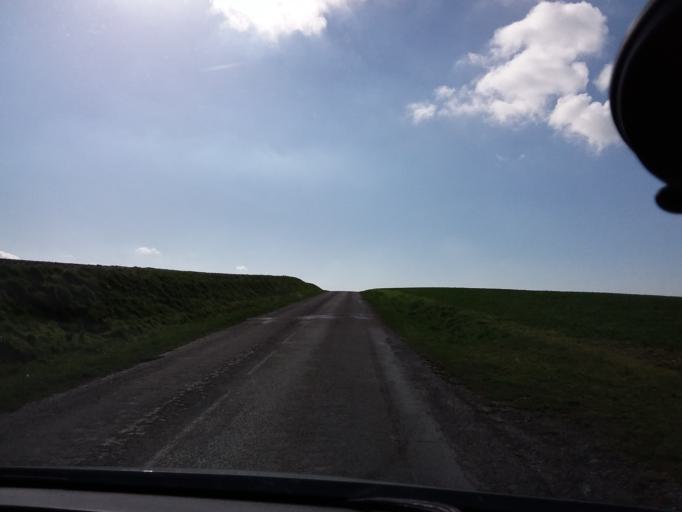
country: FR
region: Picardie
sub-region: Departement de l'Aisne
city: Montcornet
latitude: 49.7931
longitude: 4.0090
